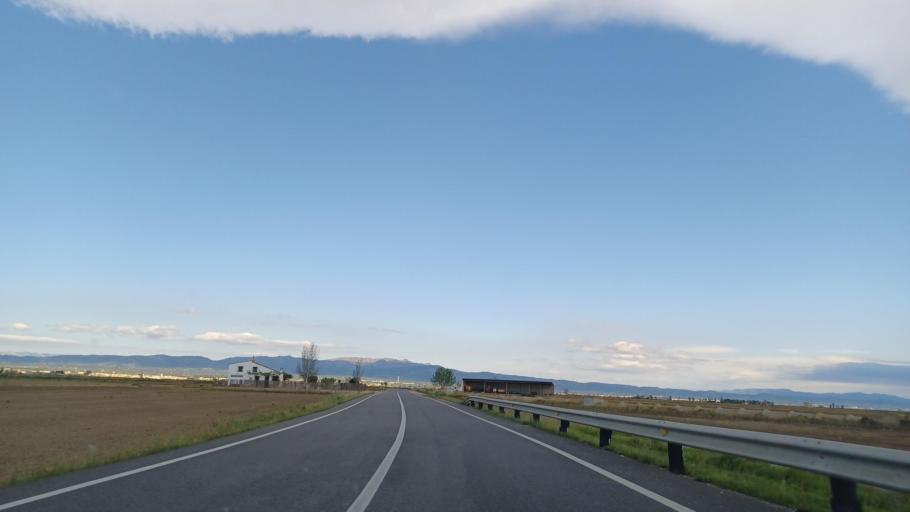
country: ES
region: Catalonia
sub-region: Provincia de Tarragona
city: Deltebre
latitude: 40.7382
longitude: 0.7140
